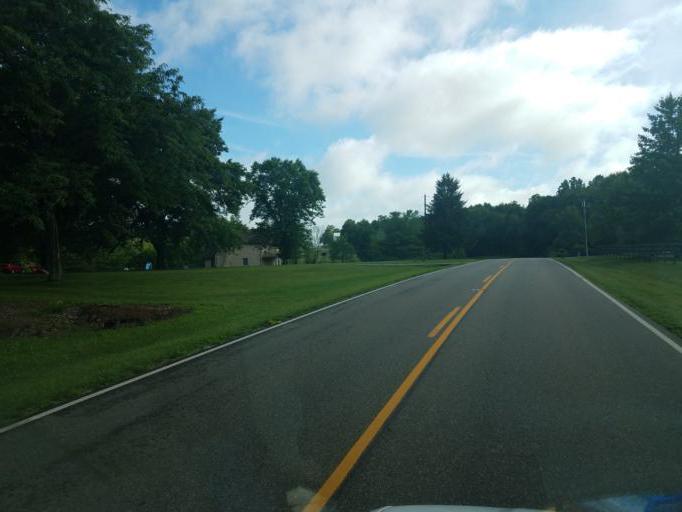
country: US
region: Ohio
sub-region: Gallia County
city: Gallipolis
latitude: 38.8548
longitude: -82.3865
